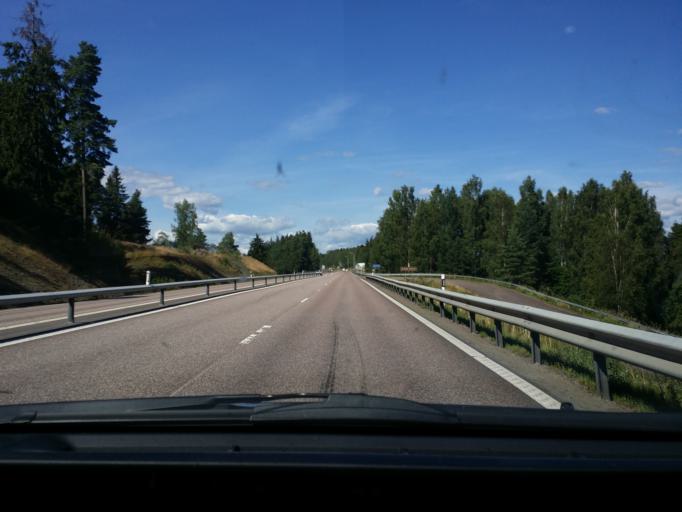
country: SE
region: Dalarna
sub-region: Hedemora Kommun
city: Brunna
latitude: 60.2377
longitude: 16.0304
